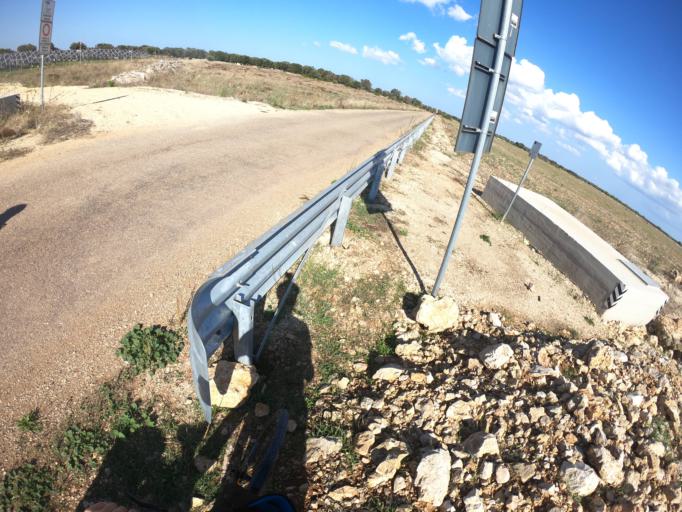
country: IT
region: Apulia
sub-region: Provincia di Lecce
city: Leverano
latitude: 40.2273
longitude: 17.9696
